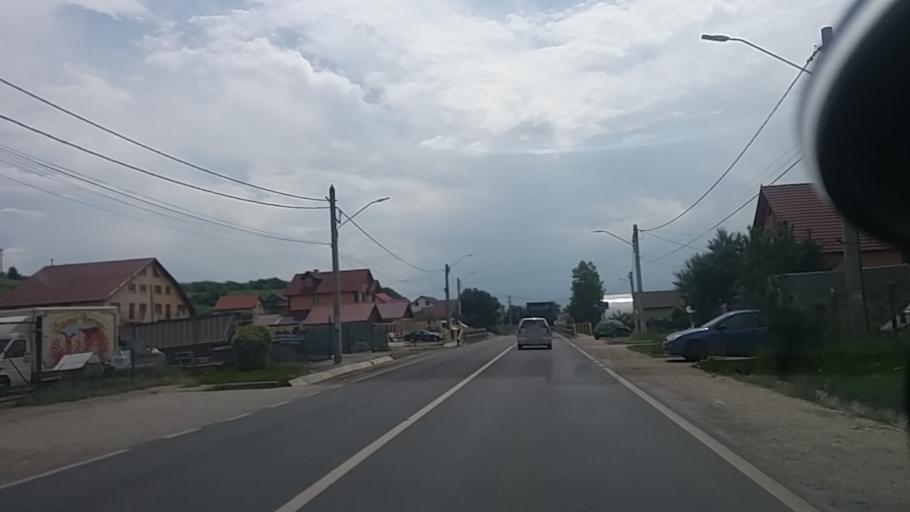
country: RO
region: Sibiu
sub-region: Comuna Sura Mare
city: Sura Mare
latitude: 45.8464
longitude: 24.1528
